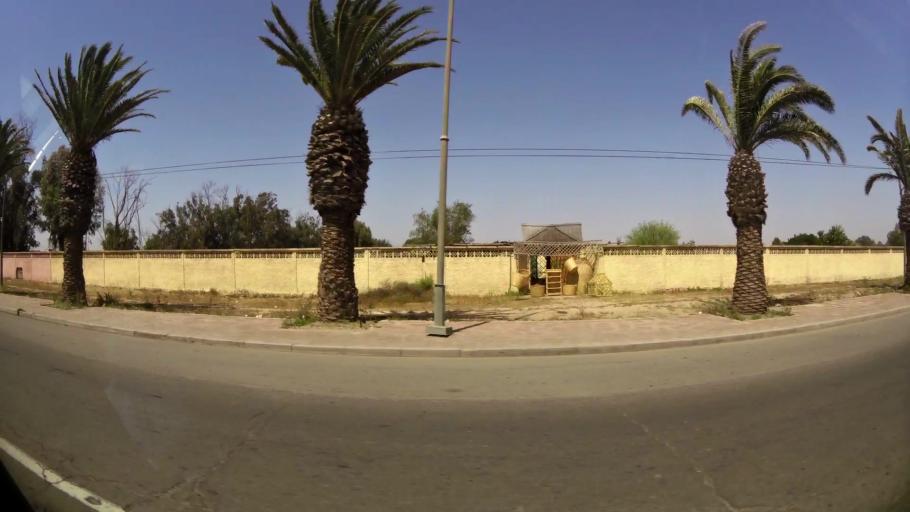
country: MA
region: Souss-Massa-Draa
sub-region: Inezgane-Ait Mellou
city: Inezgane
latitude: 30.3561
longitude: -9.5153
